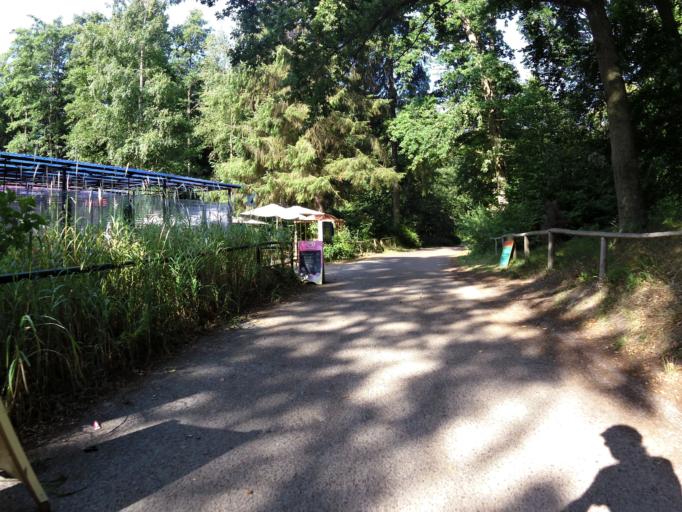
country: DE
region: Mecklenburg-Vorpommern
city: Seebad Bansin
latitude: 53.9917
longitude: 14.1133
